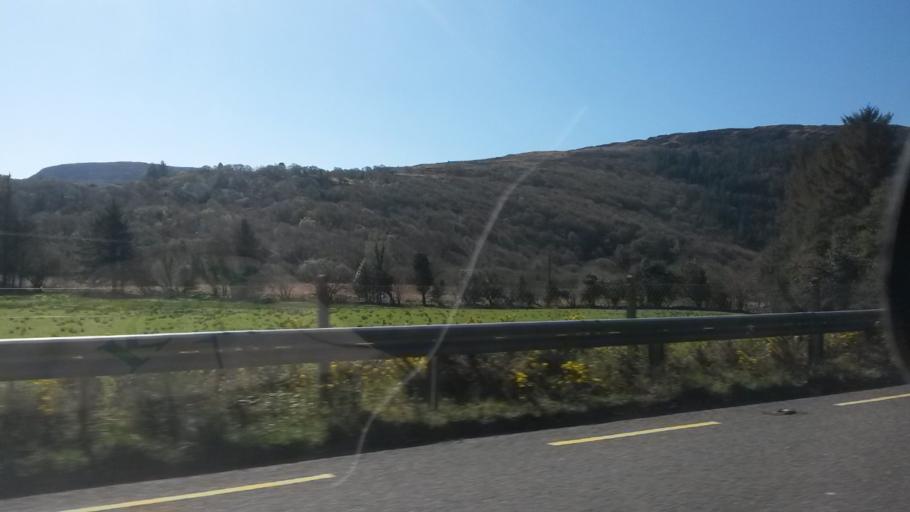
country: IE
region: Munster
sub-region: Ciarrai
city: Cill Airne
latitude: 51.9652
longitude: -9.3581
